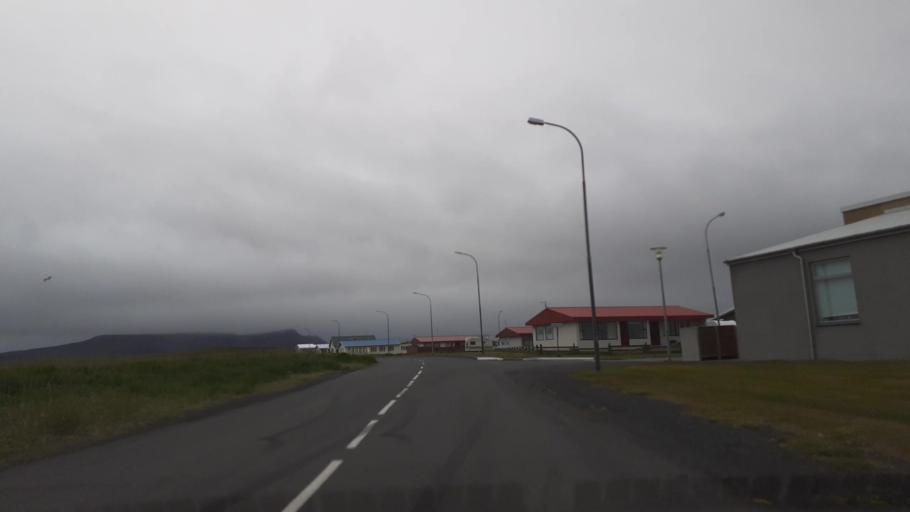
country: IS
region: Northeast
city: Husavik
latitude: 66.3010
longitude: -16.4488
